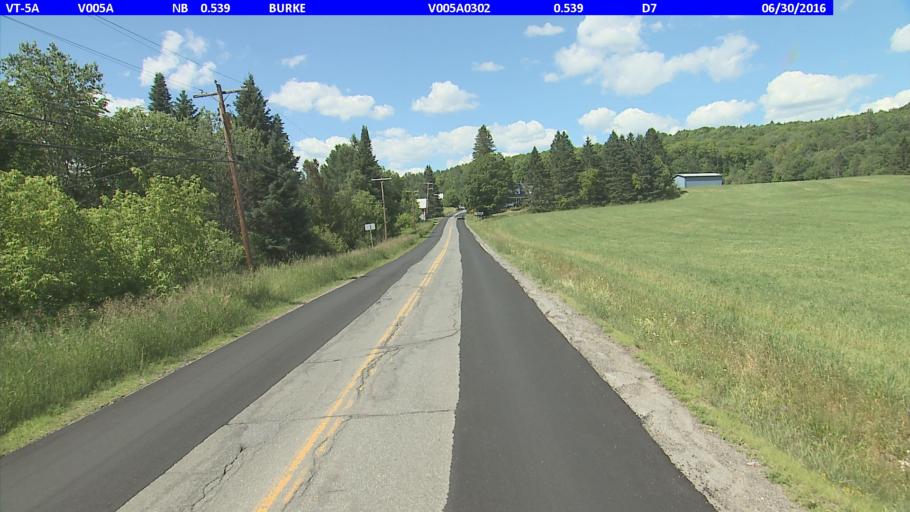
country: US
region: Vermont
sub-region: Caledonia County
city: Lyndonville
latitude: 44.6490
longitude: -71.9823
